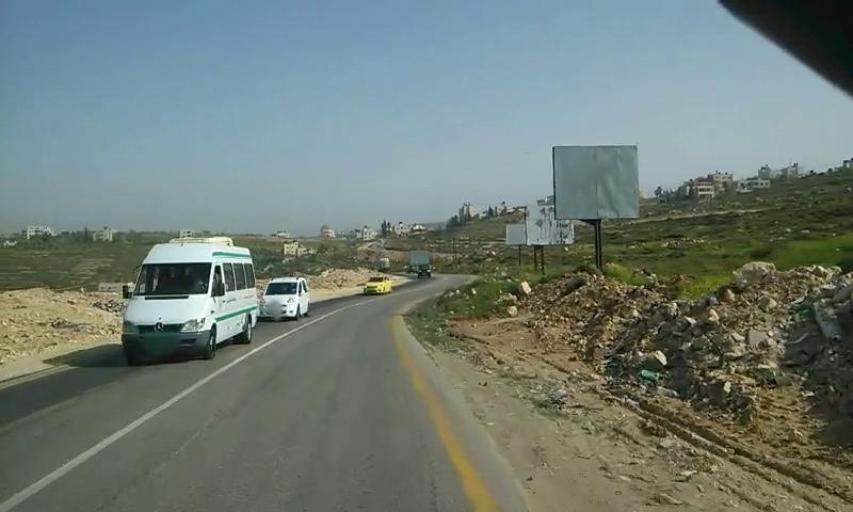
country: PS
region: West Bank
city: Surda
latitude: 31.9372
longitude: 35.2107
